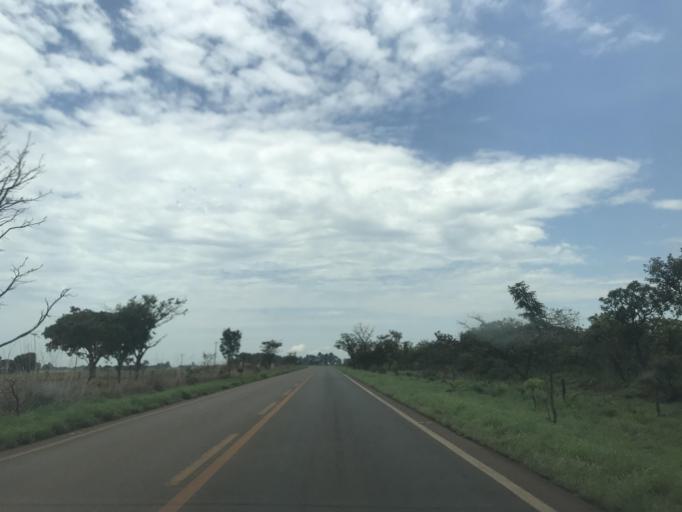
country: BR
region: Goias
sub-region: Luziania
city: Luziania
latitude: -16.2913
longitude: -48.0057
